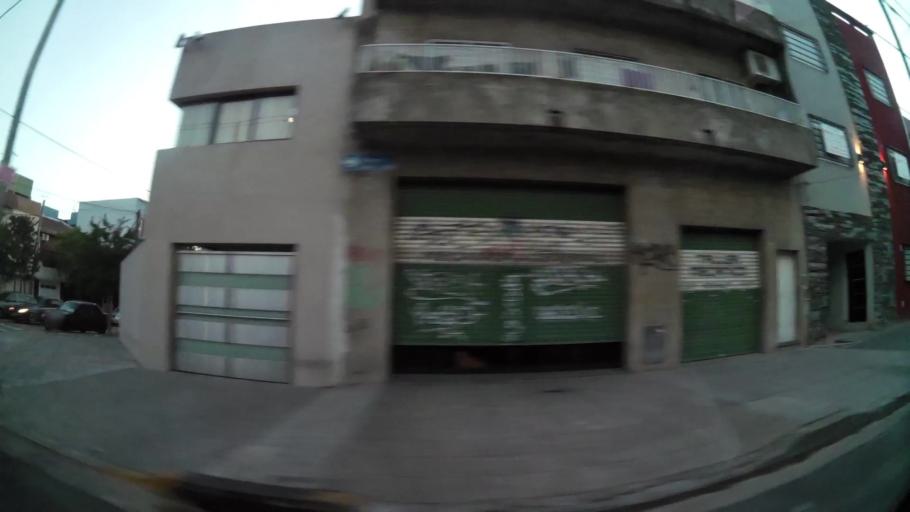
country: AR
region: Buenos Aires F.D.
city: Villa Lugano
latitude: -34.6814
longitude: -58.4731
